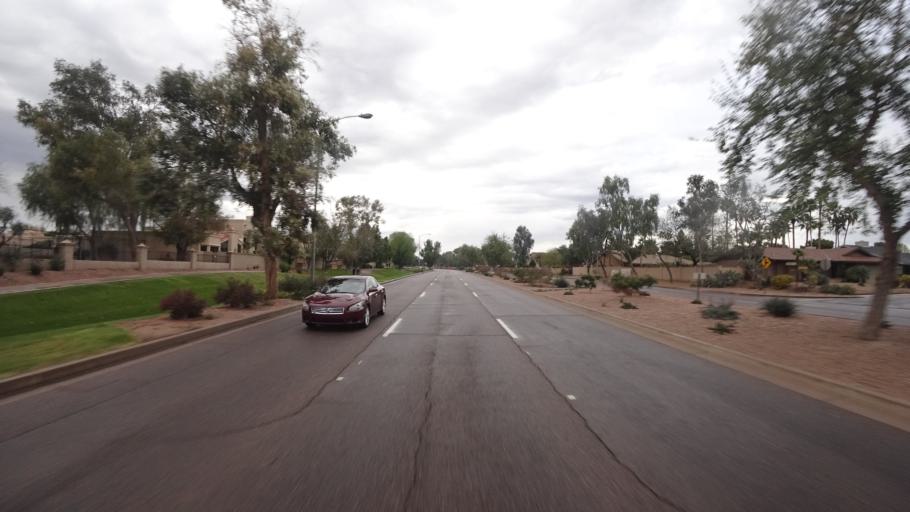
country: US
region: Arizona
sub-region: Maricopa County
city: Scottsdale
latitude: 33.5587
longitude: -111.8986
